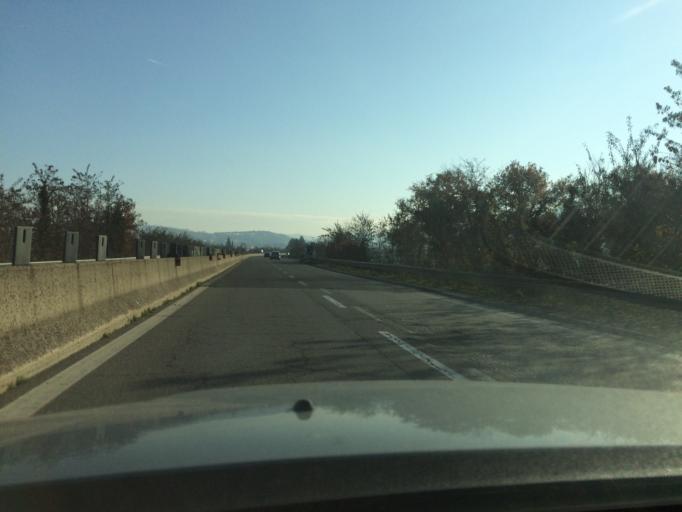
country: IT
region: Umbria
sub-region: Provincia di Perugia
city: Ponterio-Pian di Porto
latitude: 42.8160
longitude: 12.4029
